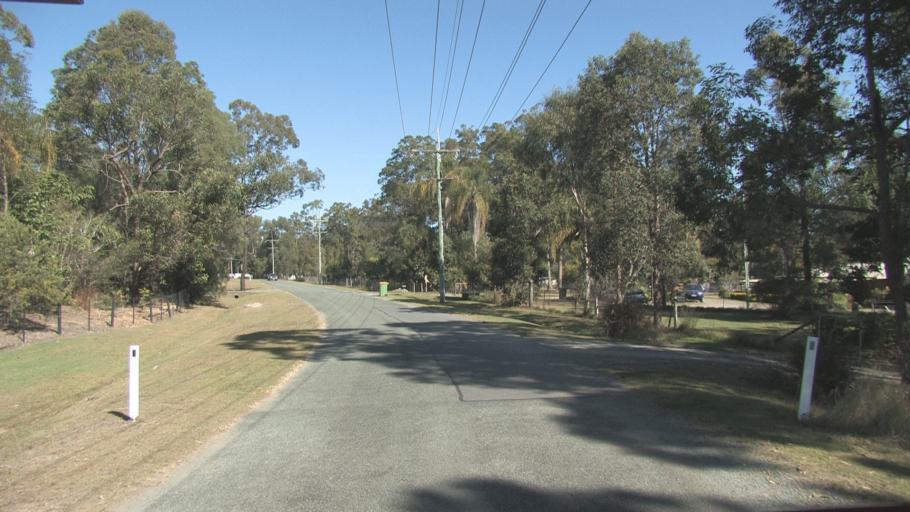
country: AU
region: Queensland
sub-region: Logan
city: Chambers Flat
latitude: -27.7771
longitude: 153.1070
